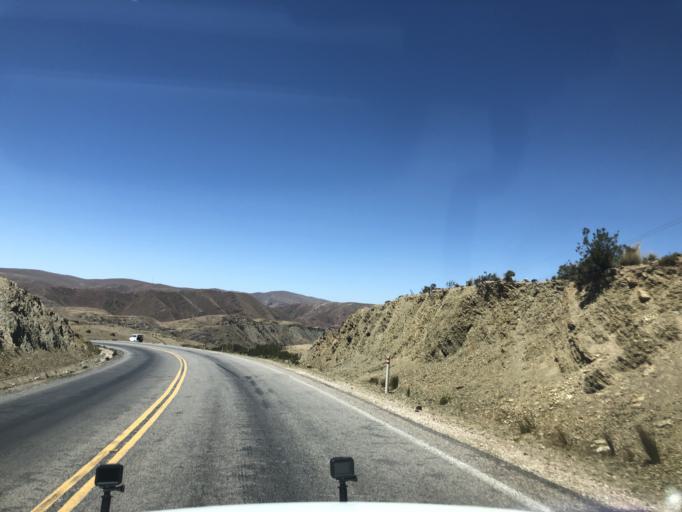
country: BO
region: Cochabamba
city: Sipe Sipe
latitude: -17.7130
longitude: -66.6568
